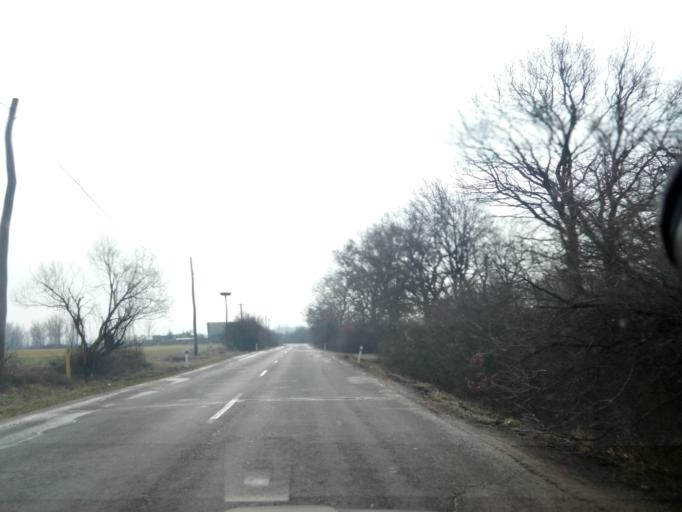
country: SK
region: Kosicky
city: Secovce
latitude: 48.6255
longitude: 21.5876
